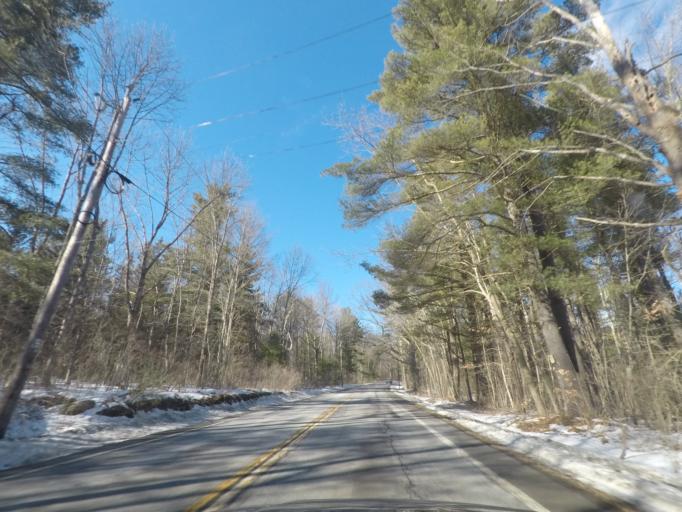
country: US
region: Massachusetts
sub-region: Berkshire County
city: West Stockbridge
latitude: 42.3208
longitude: -73.4714
